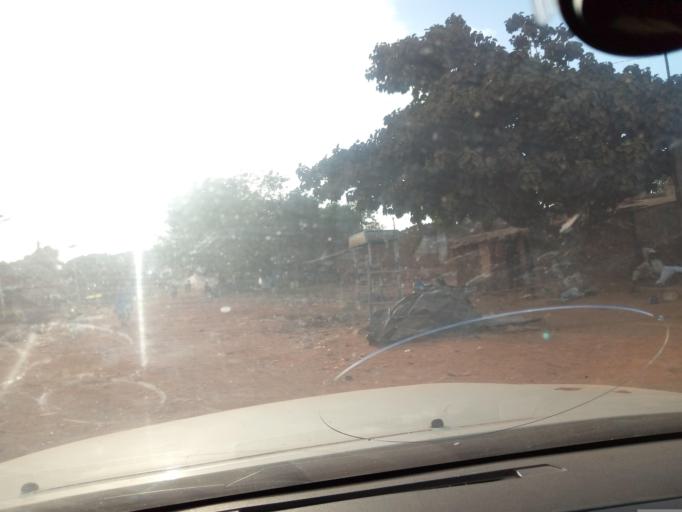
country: ML
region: Sikasso
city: Sikasso
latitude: 11.3151
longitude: -5.6456
